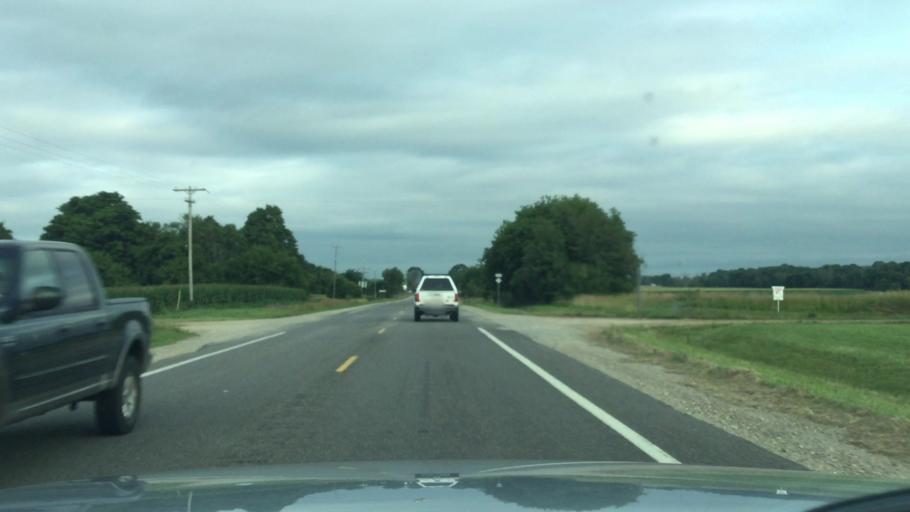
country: US
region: Michigan
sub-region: Montcalm County
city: Stanton
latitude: 43.1781
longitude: -85.0536
